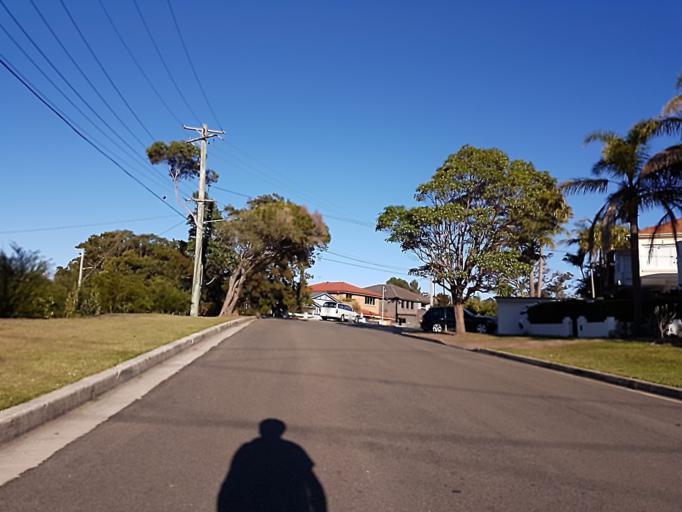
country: AU
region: New South Wales
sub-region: Manly Vale
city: Balgowlah
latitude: -33.7914
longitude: 151.2544
